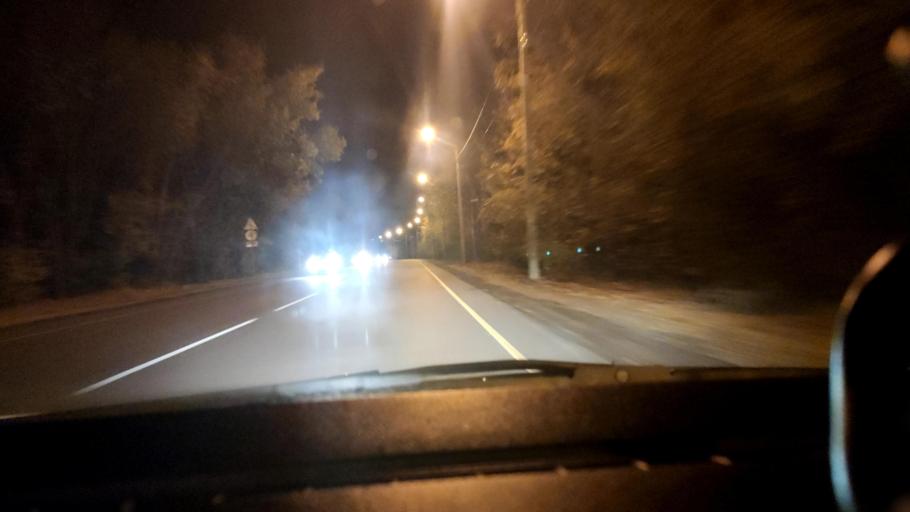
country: RU
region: Voronezj
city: Voronezh
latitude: 51.6021
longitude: 39.1776
